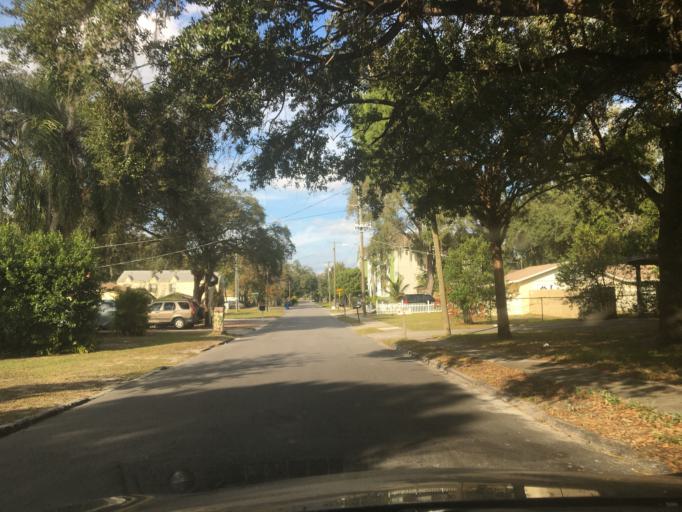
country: US
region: Florida
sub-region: Hillsborough County
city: Temple Terrace
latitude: 28.0298
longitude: -82.4145
